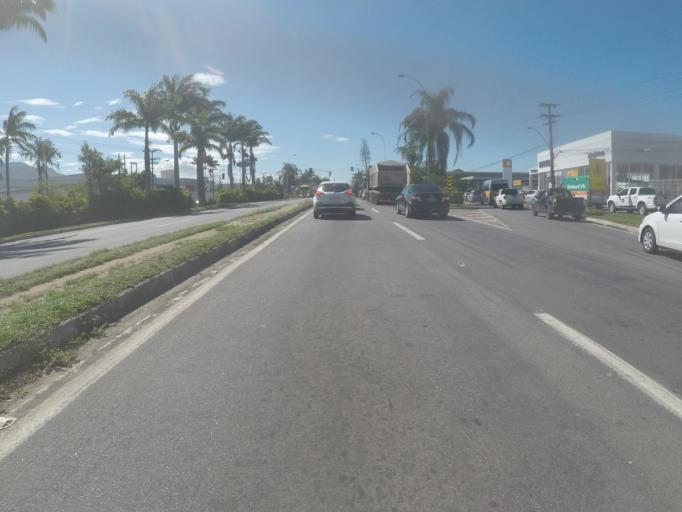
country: BR
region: Espirito Santo
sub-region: Serra
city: Serra
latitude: -20.2081
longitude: -40.2694
